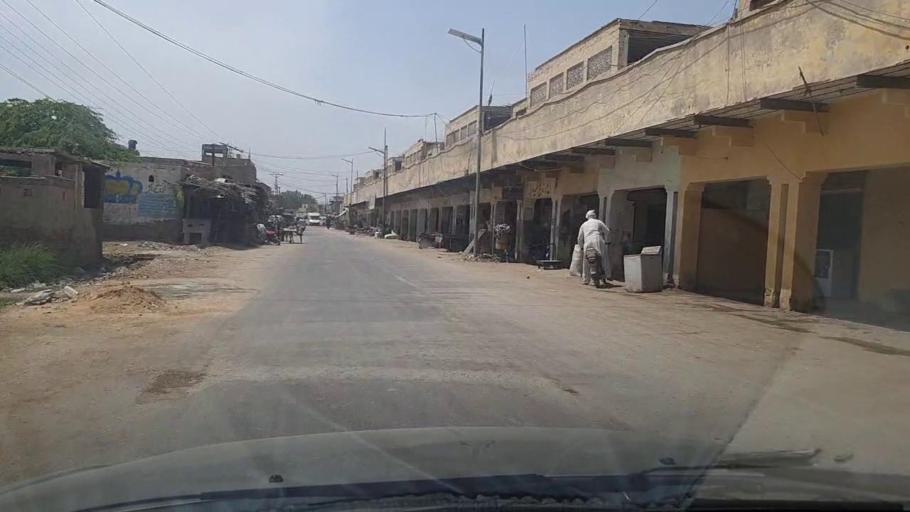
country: PK
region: Sindh
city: Bhiria
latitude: 26.9071
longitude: 68.1974
